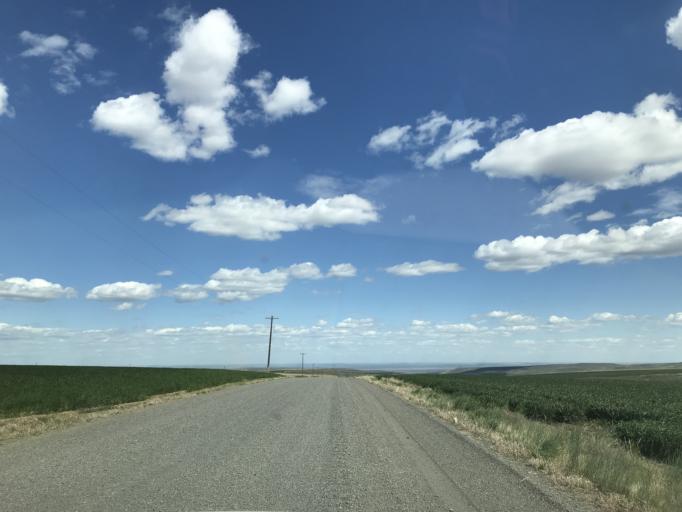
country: US
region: Washington
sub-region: Grant County
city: Ephrata
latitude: 47.3374
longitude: -119.7119
